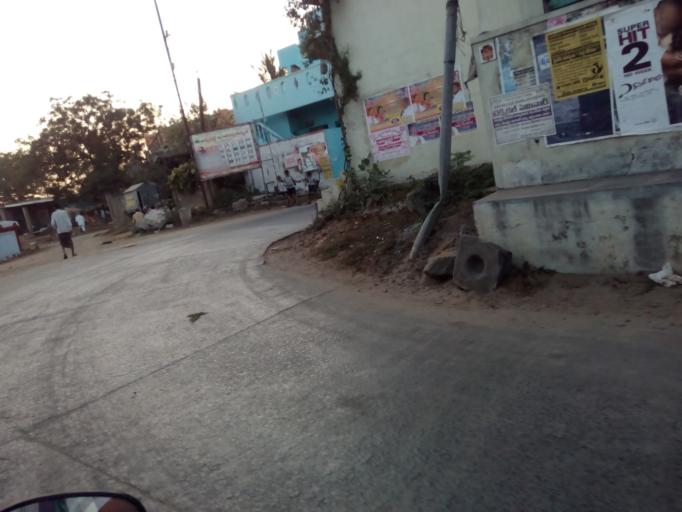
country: IN
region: Andhra Pradesh
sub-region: Prakasam
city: Vetapalem
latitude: 15.7265
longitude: 80.2544
